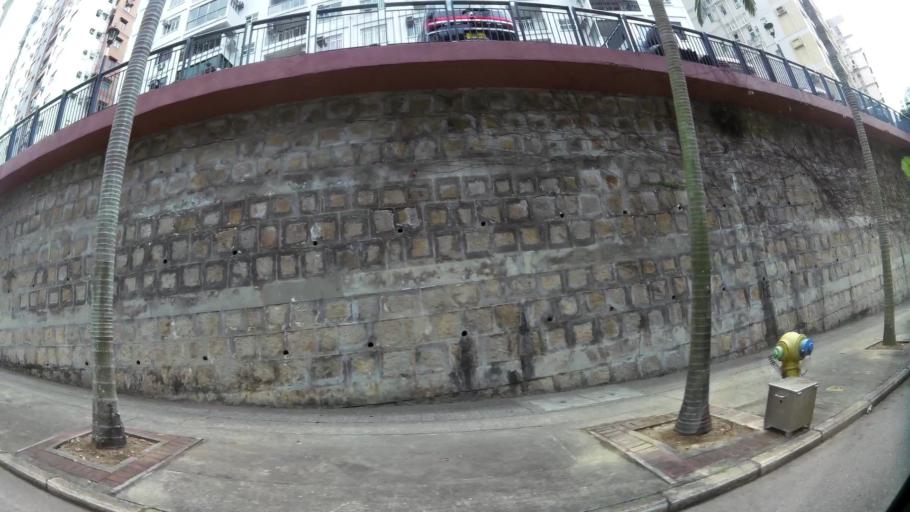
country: HK
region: Wanchai
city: Wan Chai
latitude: 22.2879
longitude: 114.1965
